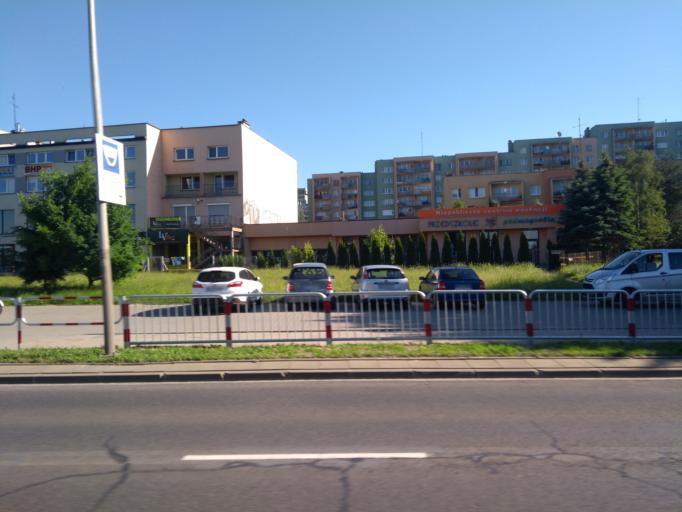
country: PL
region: Lesser Poland Voivodeship
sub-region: Krakow
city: Krakow
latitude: 50.0744
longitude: 20.0082
